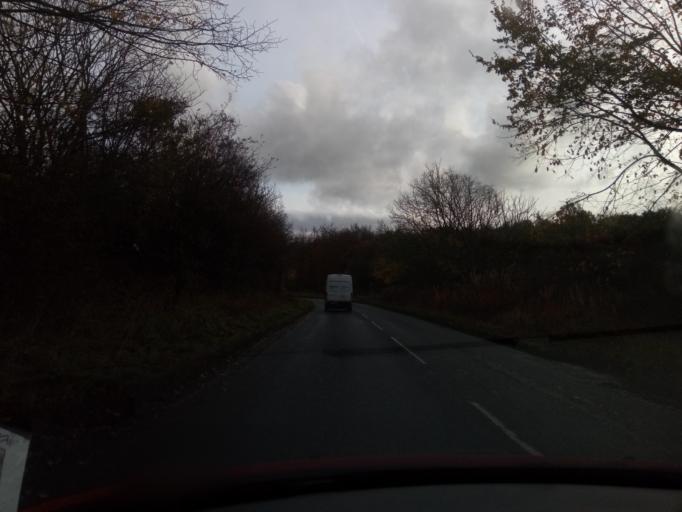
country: GB
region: England
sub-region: Northumberland
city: Birtley
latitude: 55.0556
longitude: -2.1895
